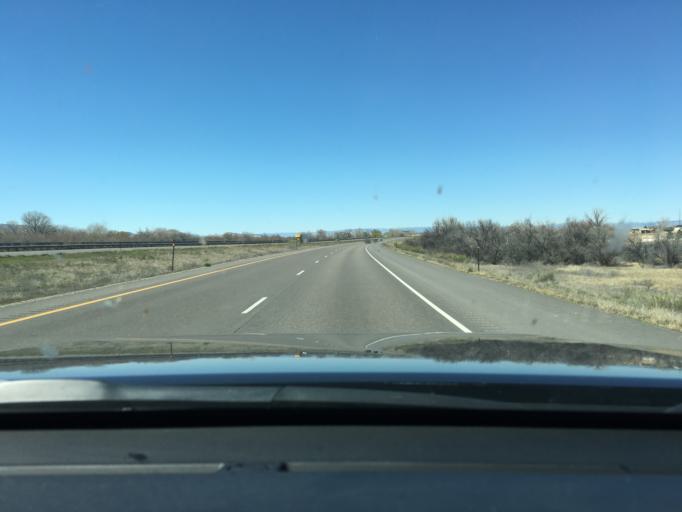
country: US
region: Colorado
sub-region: Mesa County
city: Redlands
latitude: 39.1208
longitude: -108.6755
